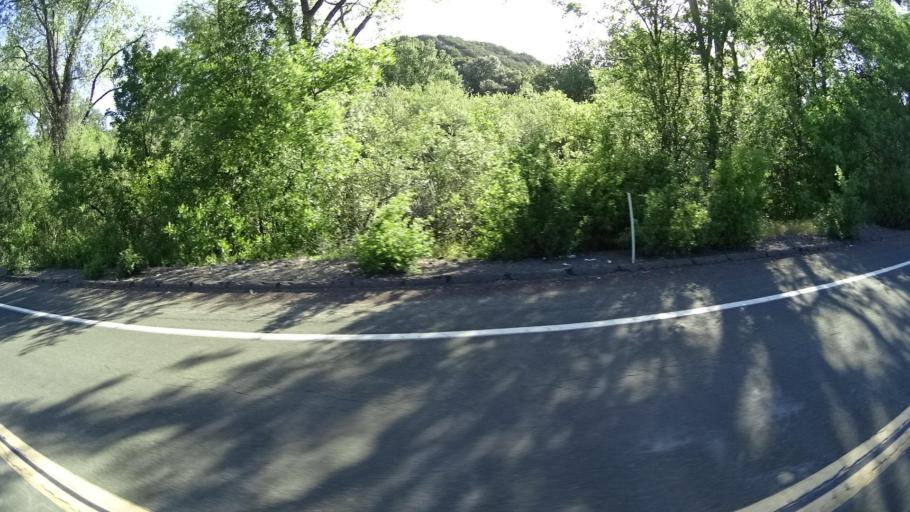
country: US
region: California
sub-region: Lake County
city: North Lakeport
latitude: 39.1071
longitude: -122.9744
